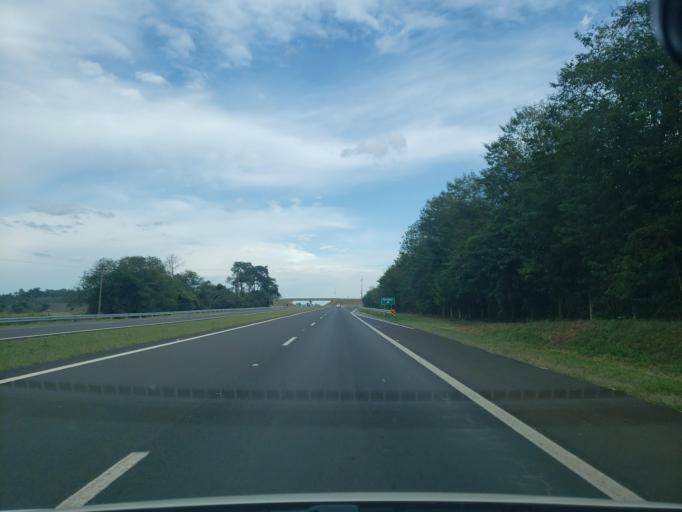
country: BR
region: Sao Paulo
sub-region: Itirapina
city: Itirapina
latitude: -22.2674
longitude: -47.9298
